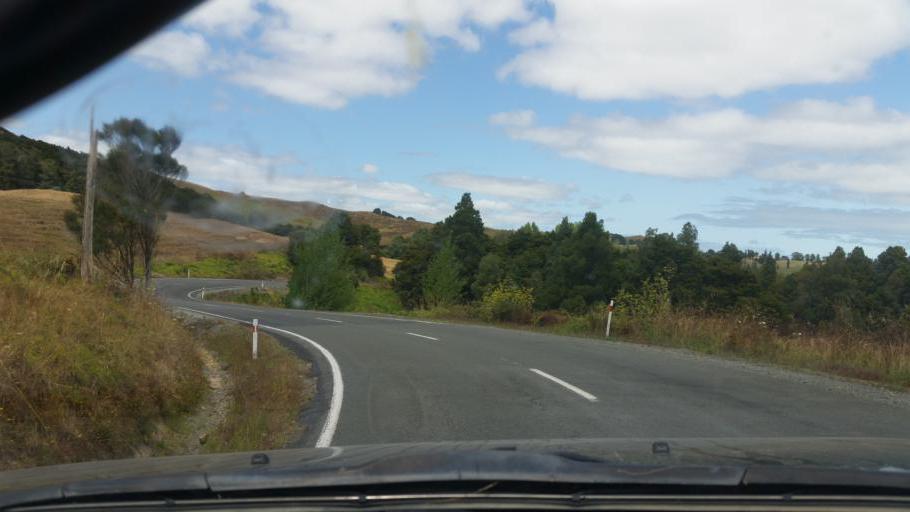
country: NZ
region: Auckland
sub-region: Auckland
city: Wellsford
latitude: -36.1261
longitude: 174.3280
